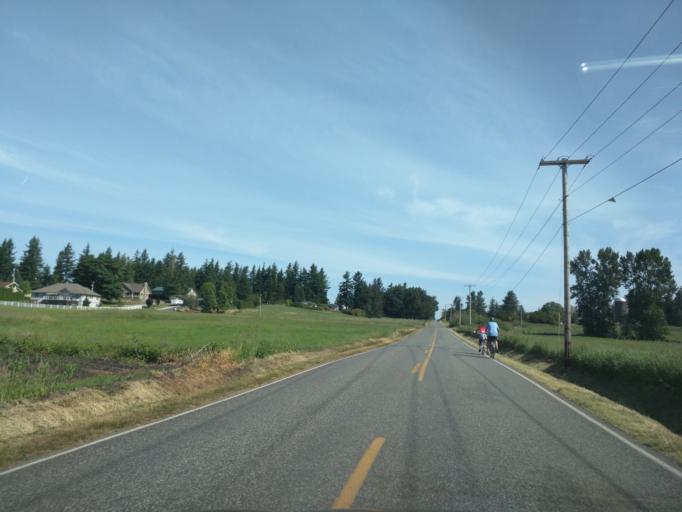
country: US
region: Washington
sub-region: Whatcom County
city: Lynden
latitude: 48.9547
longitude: -122.4078
